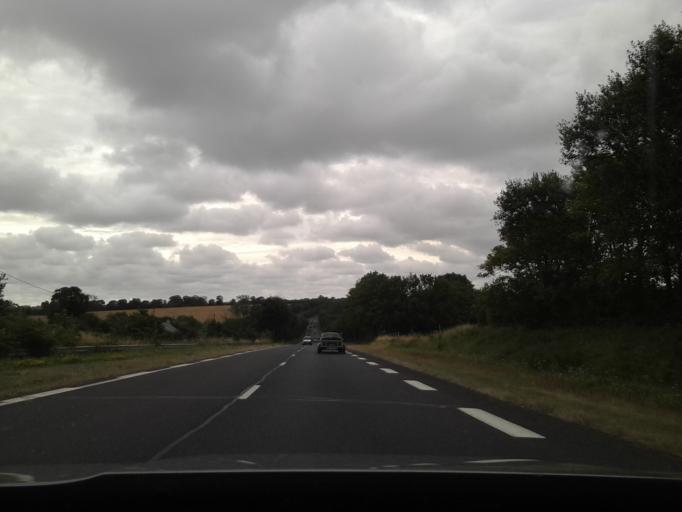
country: FR
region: Lower Normandy
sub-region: Departement du Calvados
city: Le Molay-Littry
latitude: 49.3217
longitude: -0.8629
